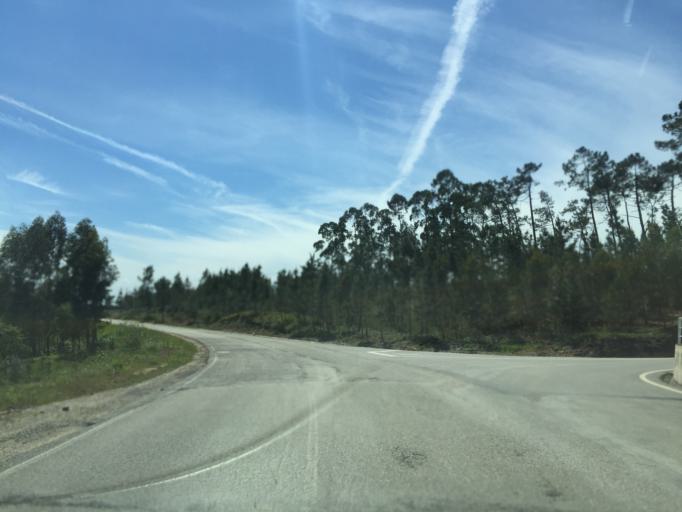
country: PT
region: Coimbra
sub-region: Soure
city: Soure
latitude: 40.0586
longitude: -8.6854
